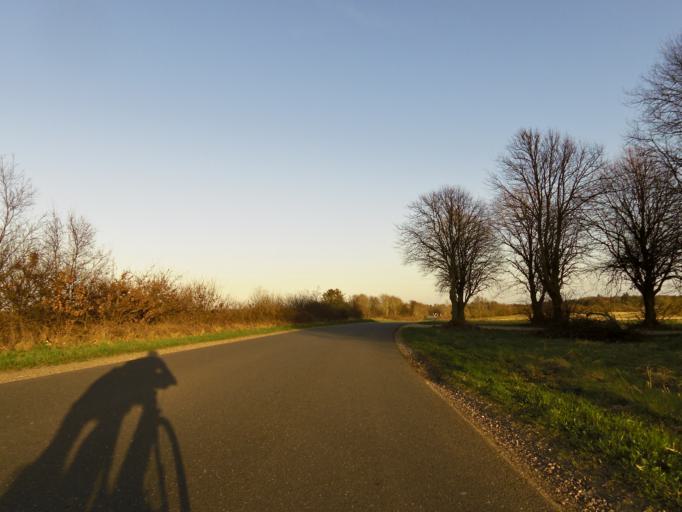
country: DK
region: Central Jutland
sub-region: Holstebro Kommune
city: Vinderup
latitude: 56.5130
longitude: 8.7983
